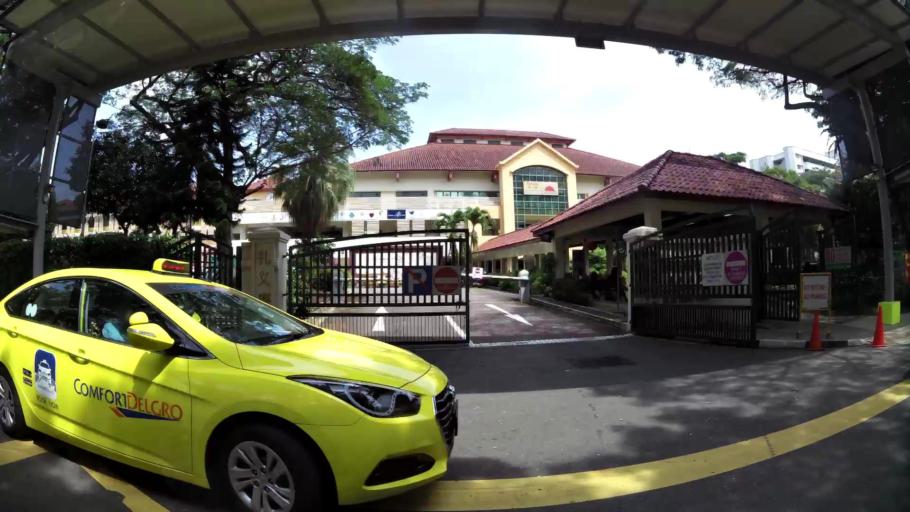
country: MY
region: Johor
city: Johor Bahru
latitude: 1.3460
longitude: 103.7189
